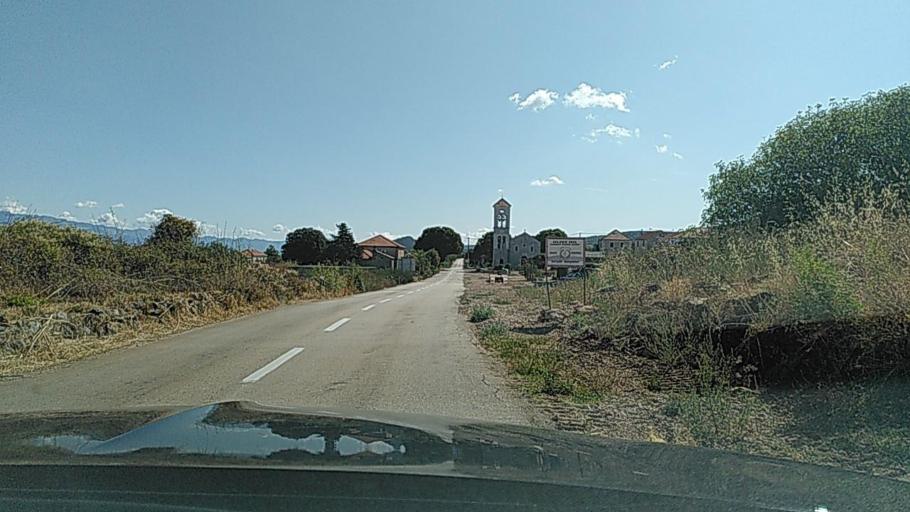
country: HR
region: Splitsko-Dalmatinska
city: Jelsa
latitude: 43.1491
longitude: 16.7915
